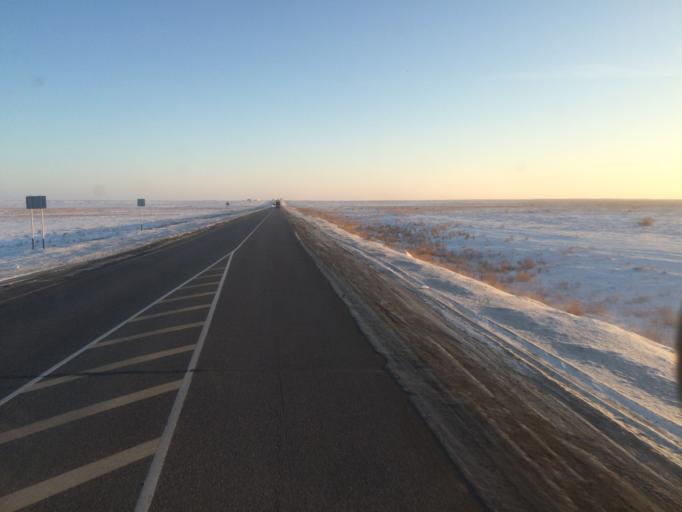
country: KZ
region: Qyzylorda
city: Sekseuil
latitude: 47.8176
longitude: 61.3402
